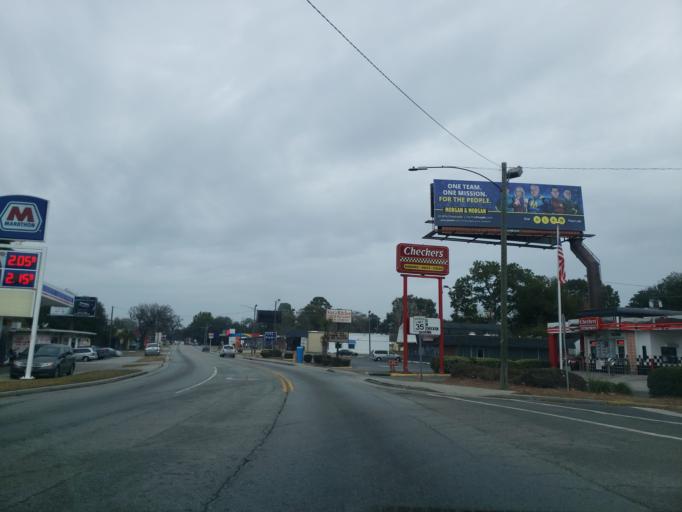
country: US
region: Georgia
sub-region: Chatham County
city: Thunderbolt
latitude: 32.0428
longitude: -81.0633
